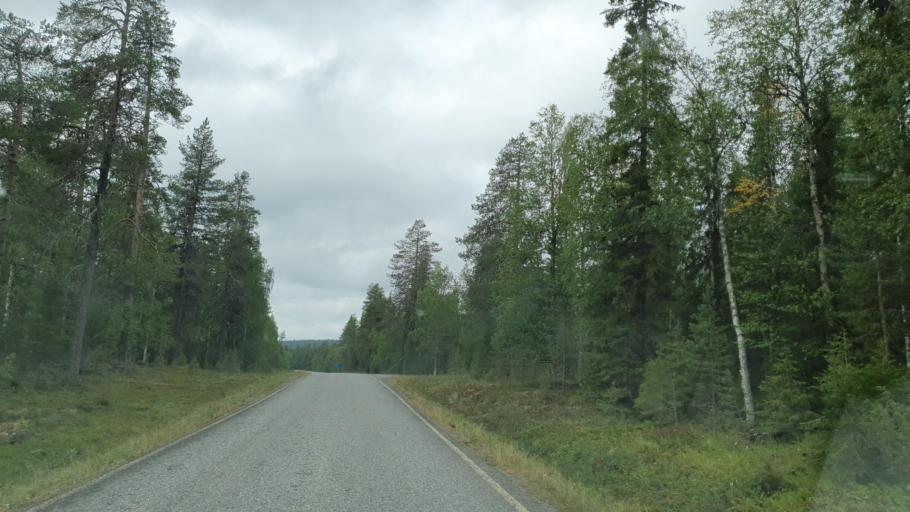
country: FI
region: Lapland
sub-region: Tunturi-Lappi
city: Kittilae
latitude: 67.7402
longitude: 24.3026
